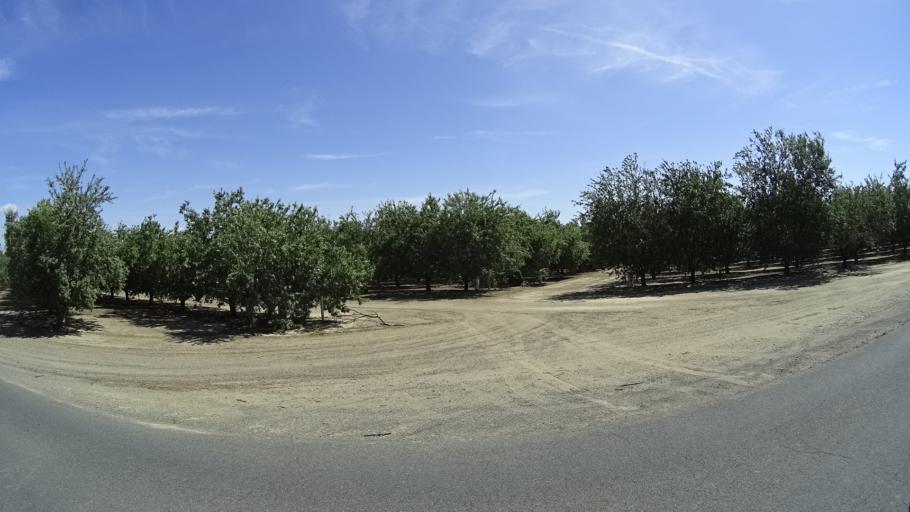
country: US
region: California
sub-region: Kings County
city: Kettleman City
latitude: 35.9698
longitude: -119.9418
